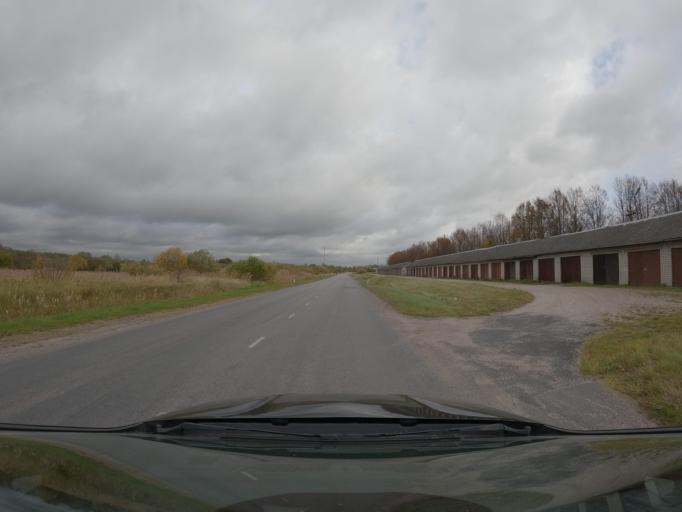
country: EE
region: Saare
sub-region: Kuressaare linn
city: Kuressaare
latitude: 58.2645
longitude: 22.4824
